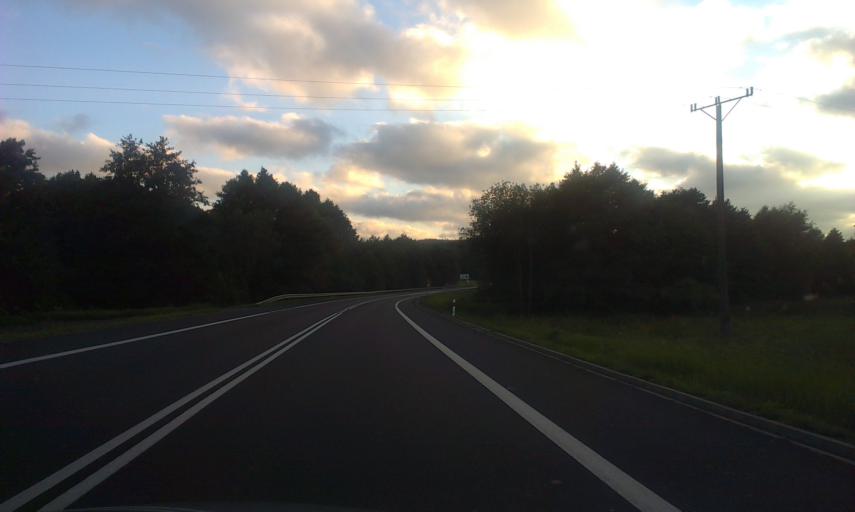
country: PL
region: West Pomeranian Voivodeship
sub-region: Powiat slawienski
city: Darlowo
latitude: 54.2784
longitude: 16.4816
